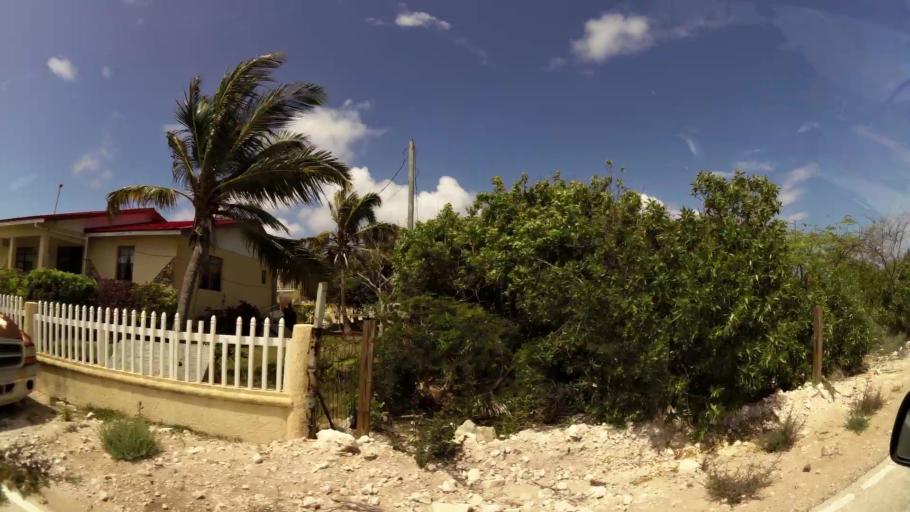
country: TC
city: Cockburn Town
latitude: 21.4916
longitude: -71.1426
